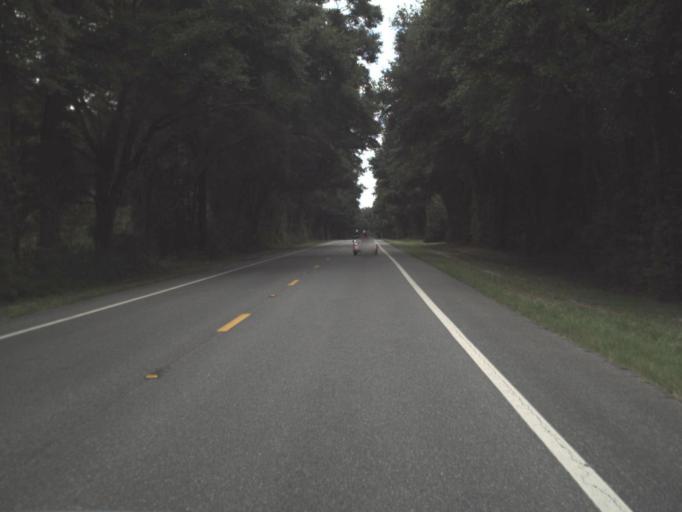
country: US
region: Florida
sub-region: Alachua County
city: Newberry
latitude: 29.6038
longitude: -82.5783
